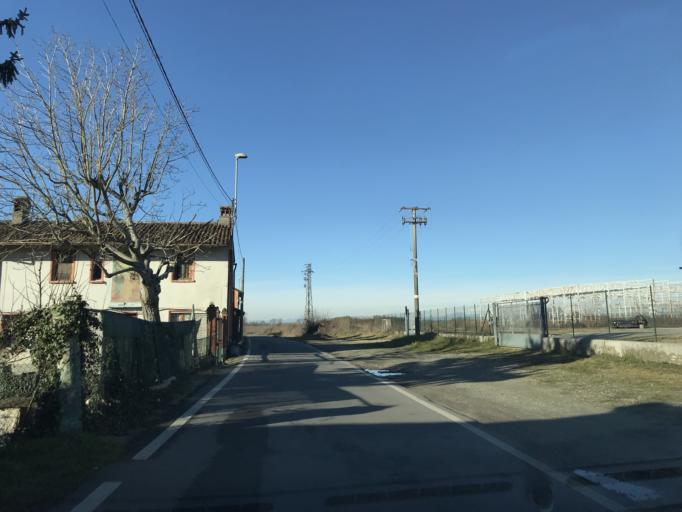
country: IT
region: Lombardy
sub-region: Provincia di Lodi
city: Graffignana
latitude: 45.2165
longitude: 9.4640
